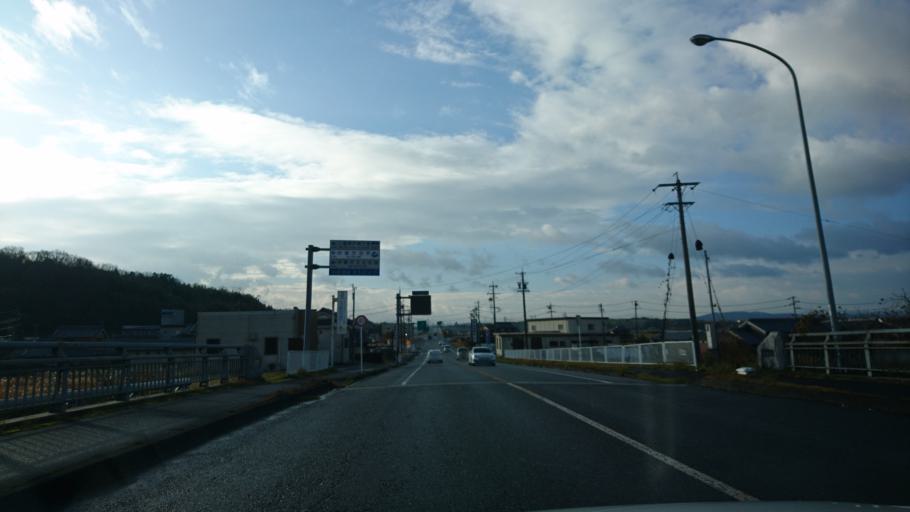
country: JP
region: Mie
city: Ueno-ebisumachi
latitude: 34.7520
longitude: 136.1228
